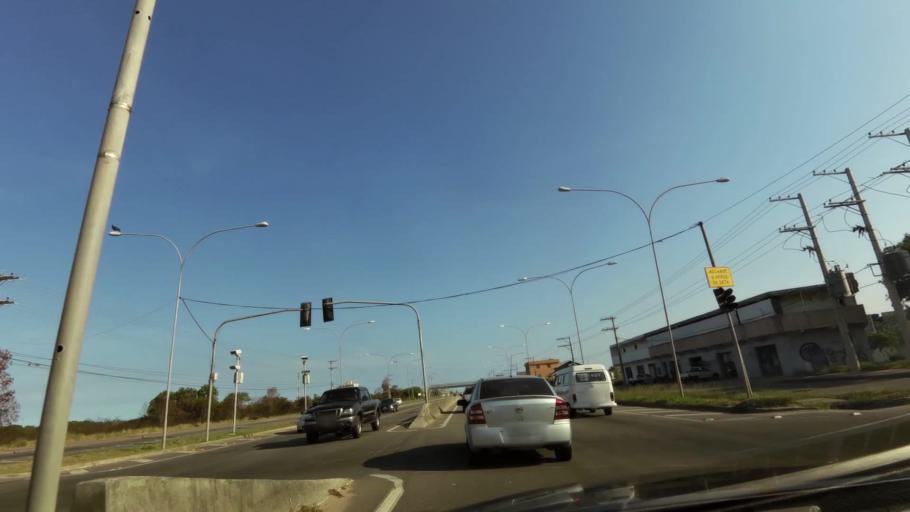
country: BR
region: Espirito Santo
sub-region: Vila Velha
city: Vila Velha
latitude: -20.4356
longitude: -40.3317
